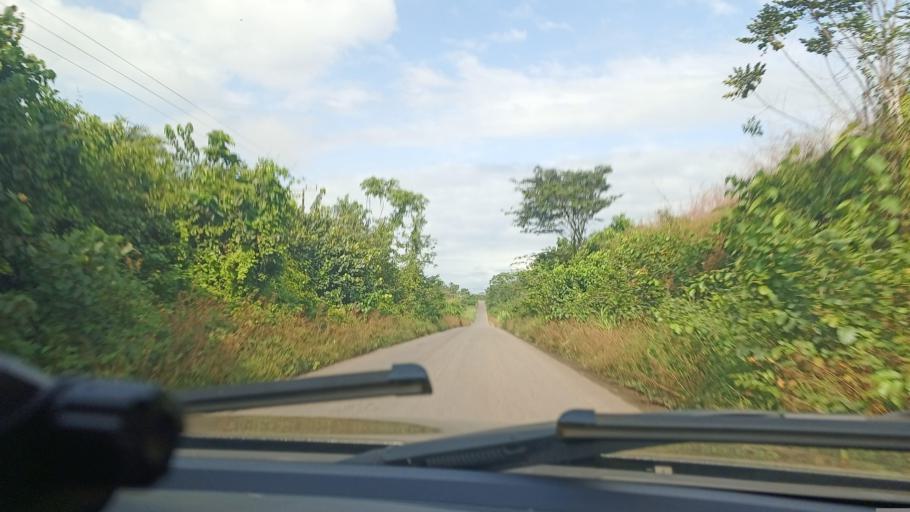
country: LR
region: Bomi
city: Tubmanburg
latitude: 6.6944
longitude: -10.8985
